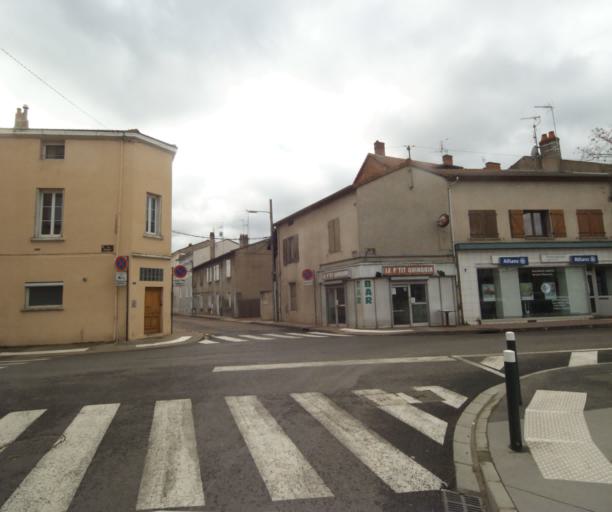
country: FR
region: Rhone-Alpes
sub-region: Departement de la Loire
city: Roanne
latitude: 46.0378
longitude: 4.0615
